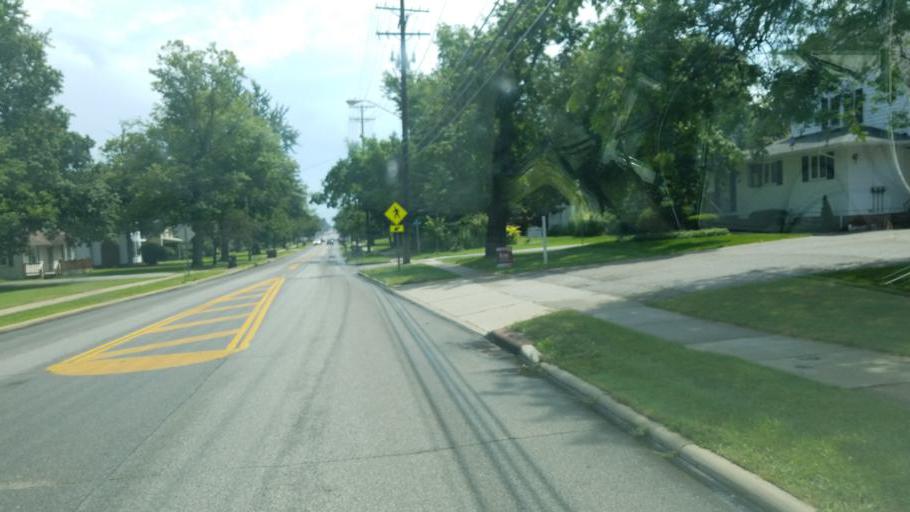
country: US
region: Ohio
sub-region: Geauga County
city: Middlefield
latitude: 41.4624
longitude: -81.0788
